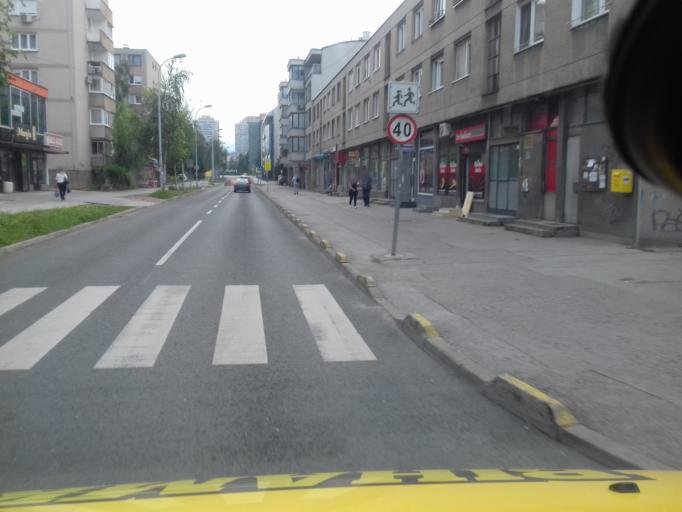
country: BA
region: Federation of Bosnia and Herzegovina
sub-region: Kanton Sarajevo
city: Sarajevo
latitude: 43.8479
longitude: 18.3699
